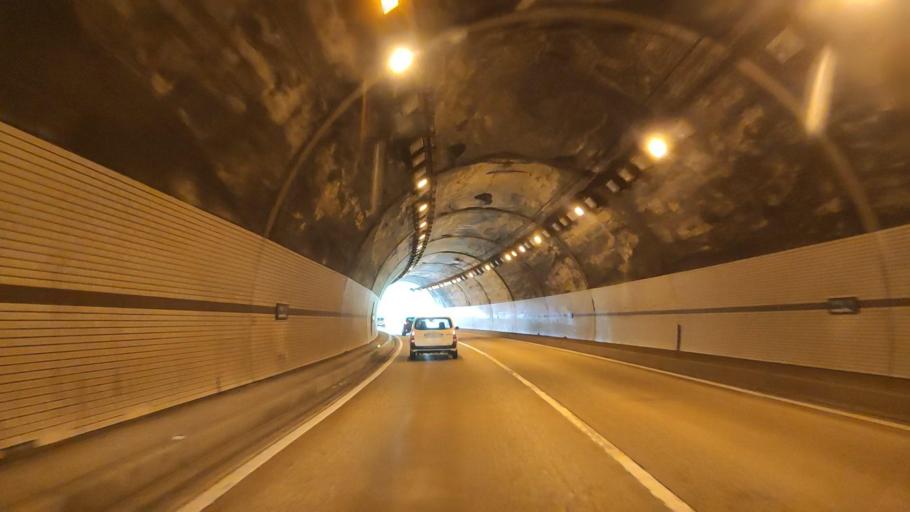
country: JP
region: Toyama
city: Yatsuomachi-higashikumisaka
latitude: 36.5040
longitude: 137.2328
